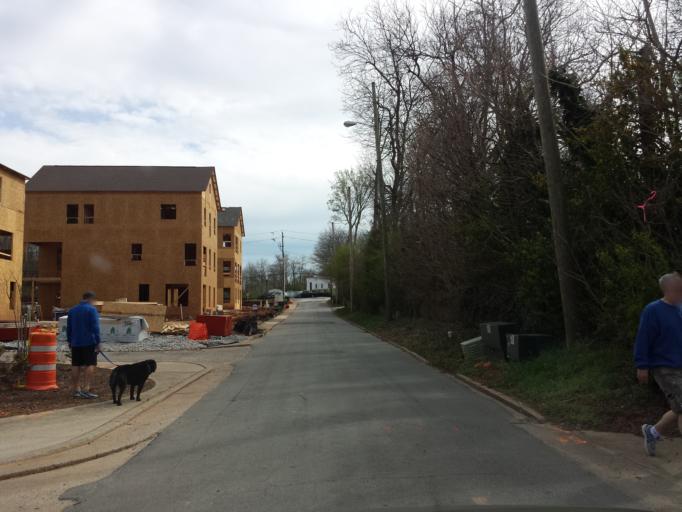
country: US
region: Georgia
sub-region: Cobb County
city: Marietta
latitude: 33.9497
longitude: -84.5480
